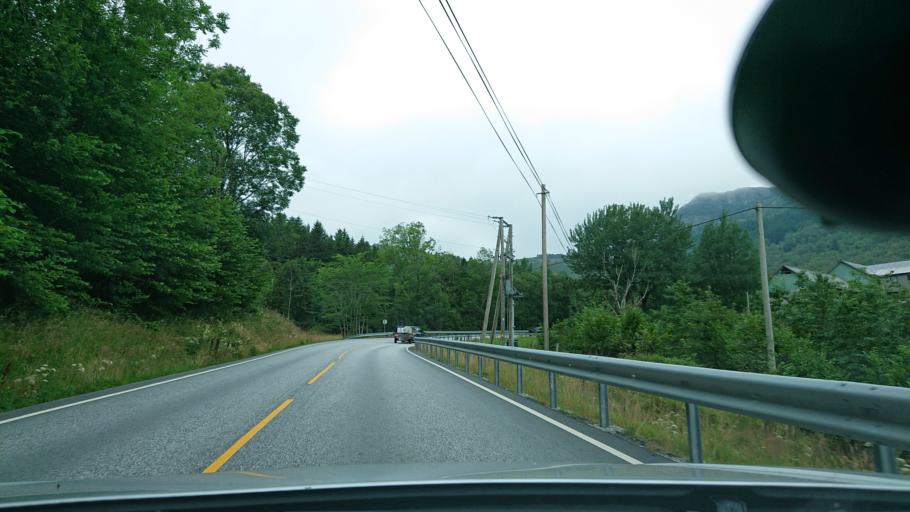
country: NO
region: Rogaland
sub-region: Hjelmeland
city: Hjelmelandsvagen
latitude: 59.1659
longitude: 6.1685
